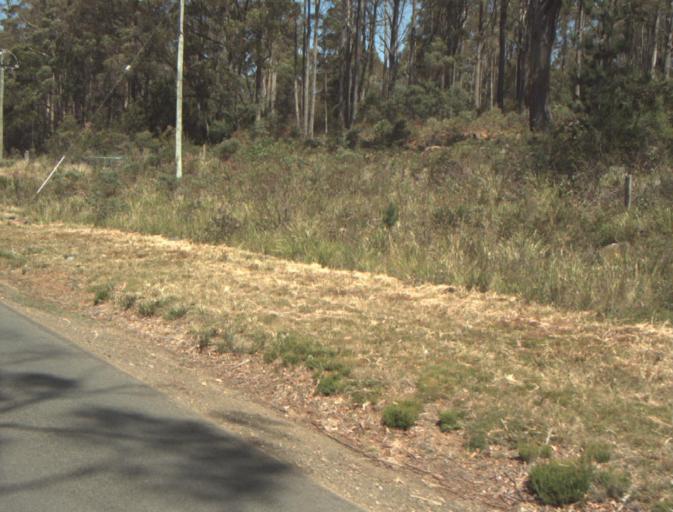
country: AU
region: Tasmania
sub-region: Launceston
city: Mayfield
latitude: -41.2876
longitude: 147.1280
